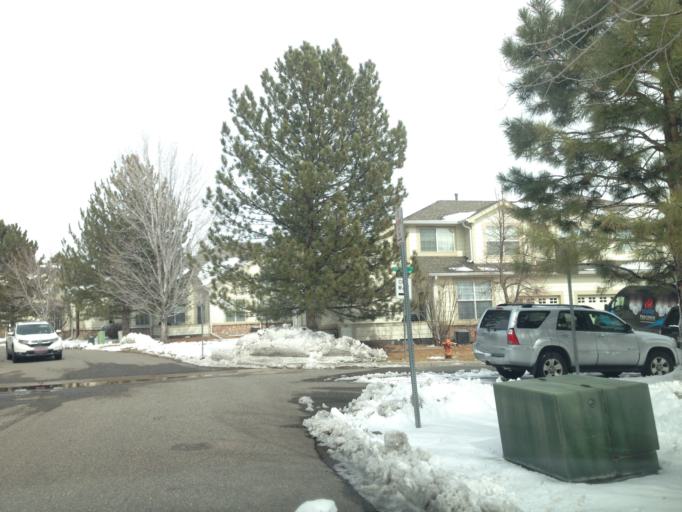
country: US
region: Colorado
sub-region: Boulder County
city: Lafayette
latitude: 39.9700
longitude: -105.0923
